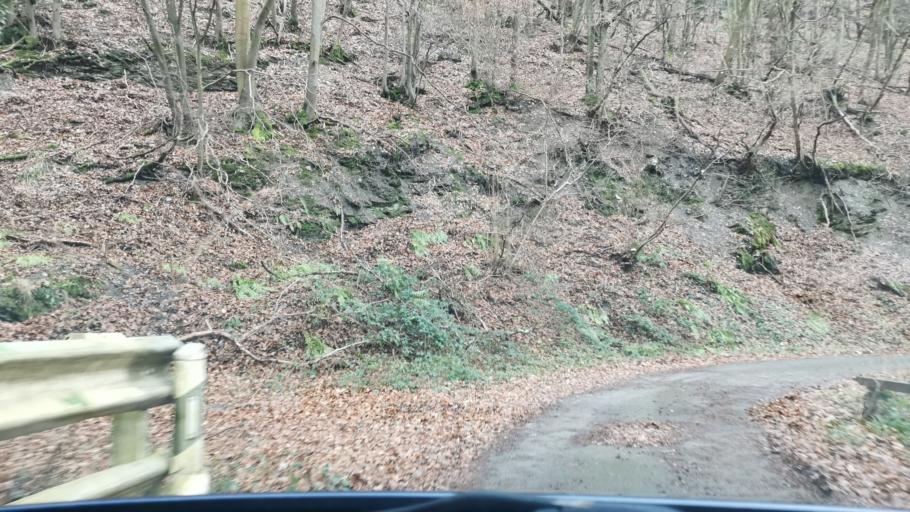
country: DE
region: Rheinland-Pfalz
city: Minheim
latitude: 49.8673
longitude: 6.9528
